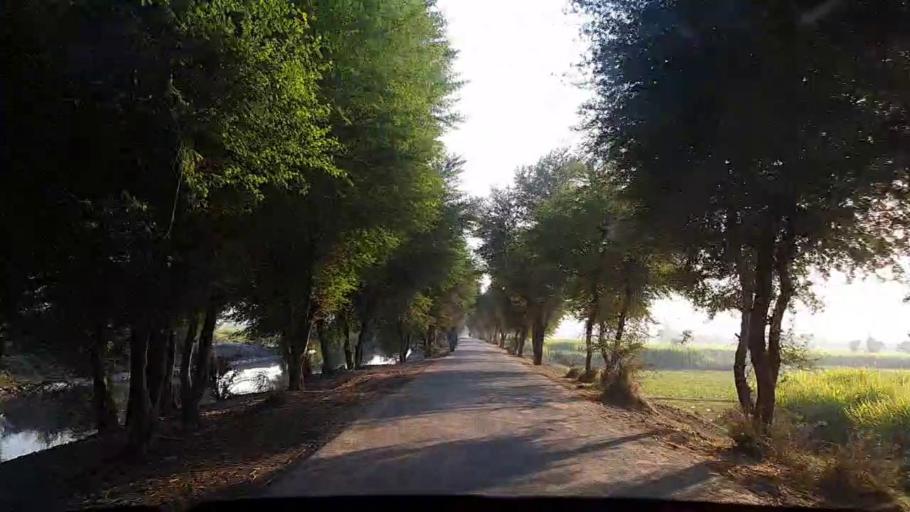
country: PK
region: Sindh
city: Sobhadero
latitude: 27.3972
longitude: 68.3875
